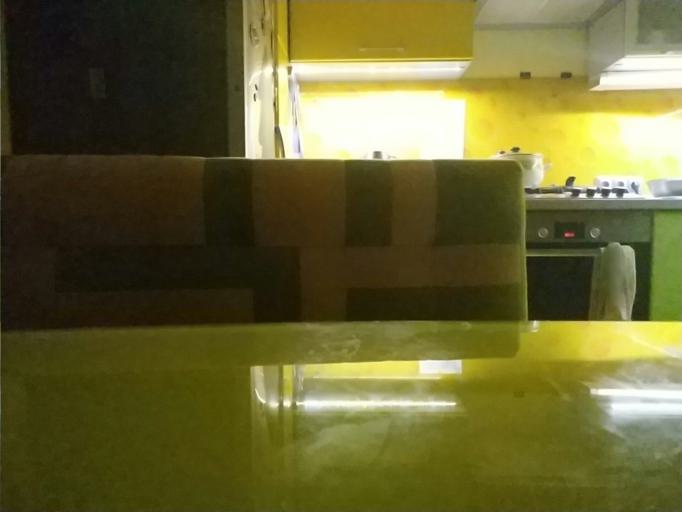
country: RU
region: Republic of Karelia
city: Pyaozerskiy
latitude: 65.4917
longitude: 30.6139
